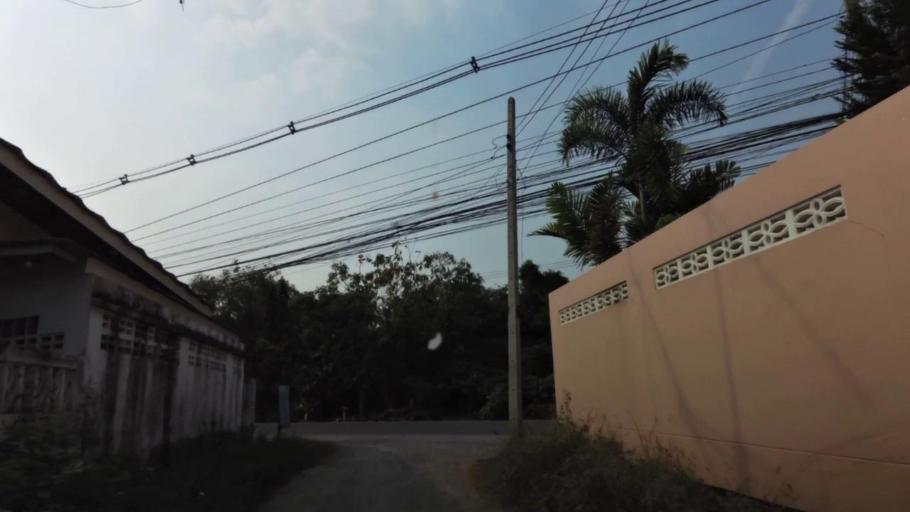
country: TH
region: Phra Nakhon Si Ayutthaya
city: Phra Nakhon Si Ayutthaya
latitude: 14.3427
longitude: 100.5666
